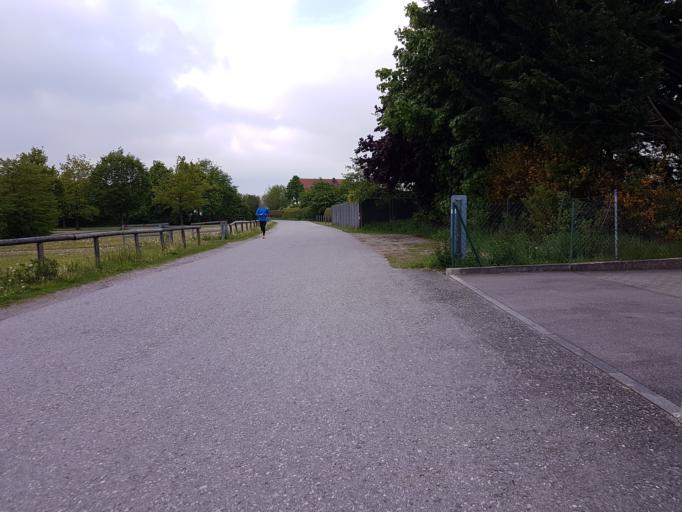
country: DE
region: Bavaria
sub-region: Upper Bavaria
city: Karlsfeld
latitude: 48.1909
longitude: 11.4544
